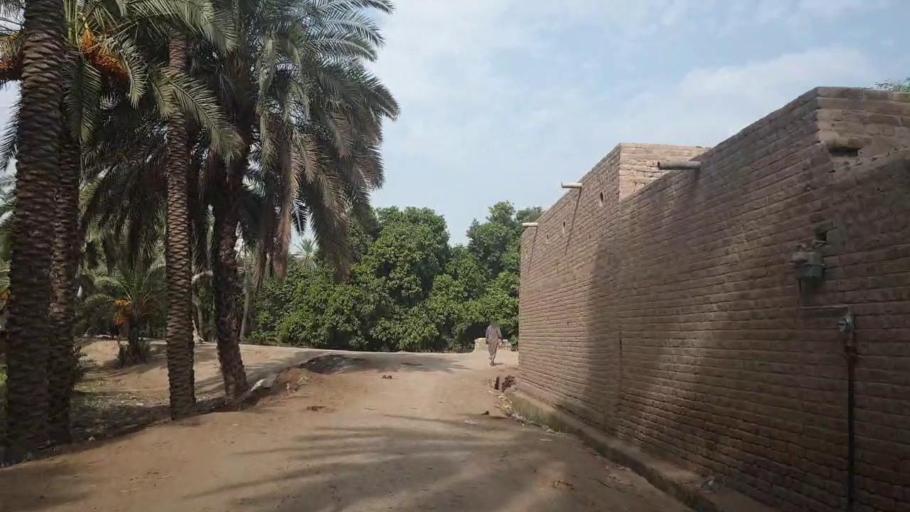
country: PK
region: Sindh
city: Sukkur
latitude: 27.6423
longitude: 68.7999
